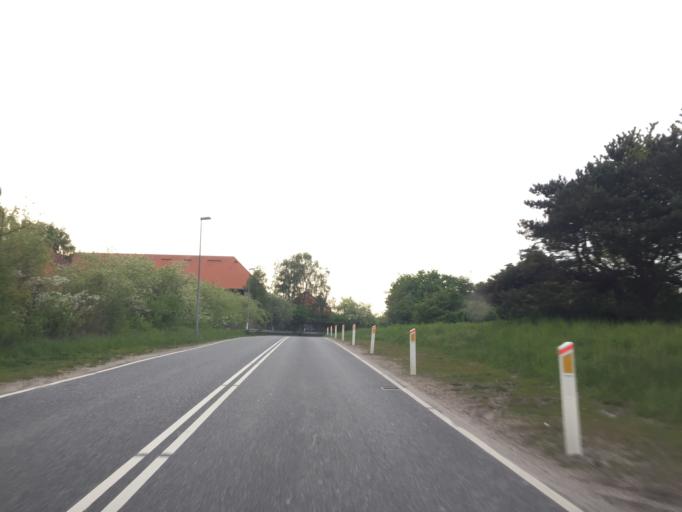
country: DK
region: Capital Region
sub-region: Rudersdal Kommune
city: Trorod
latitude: 55.8150
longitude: 12.5263
